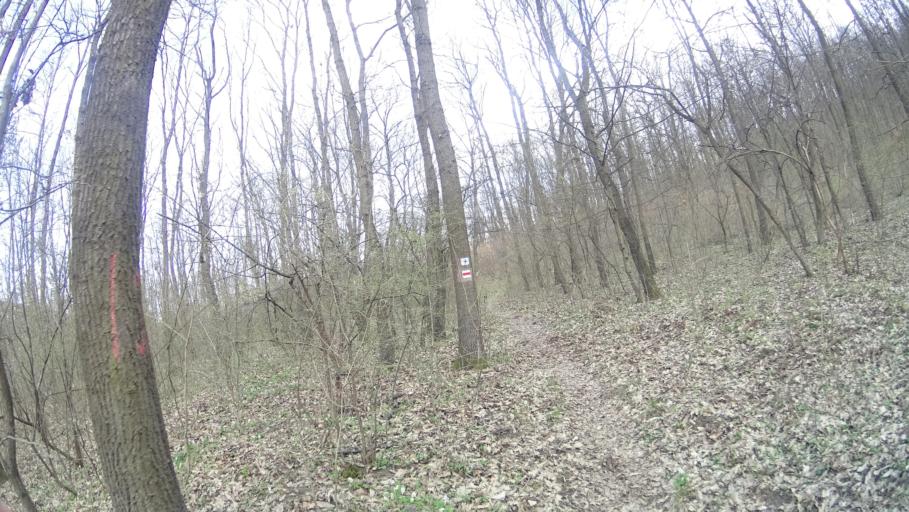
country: HU
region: Pest
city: Veroce
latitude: 47.8442
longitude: 19.1011
